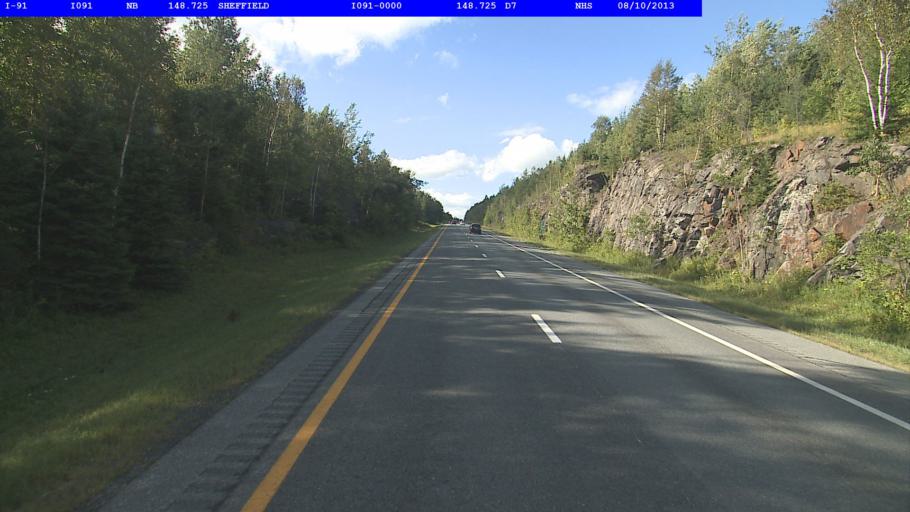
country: US
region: Vermont
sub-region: Caledonia County
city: Lyndonville
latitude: 44.6462
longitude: -72.1318
